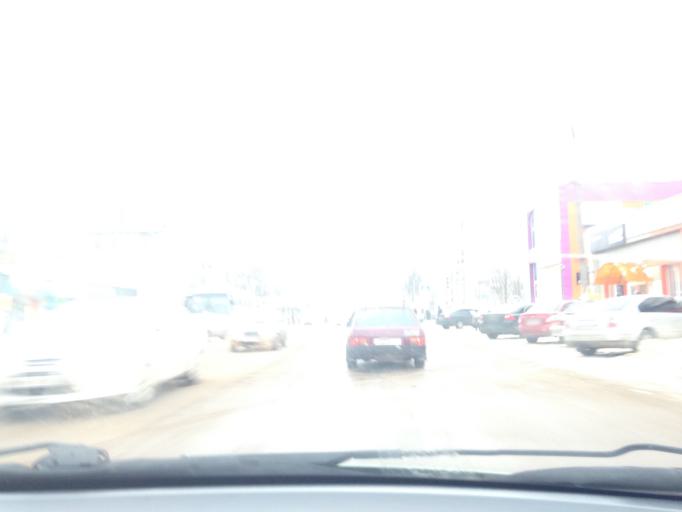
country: RU
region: Tula
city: Shchekino
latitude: 54.0117
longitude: 37.5147
